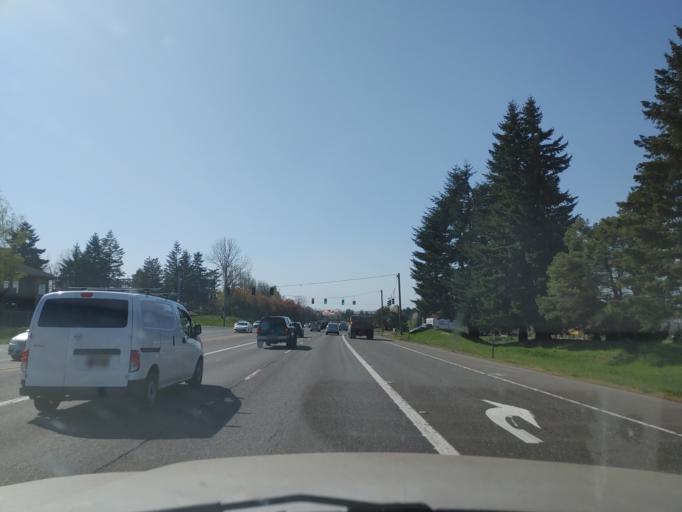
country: US
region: Oregon
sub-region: Clackamas County
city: Clackamas
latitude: 45.4225
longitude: -122.5809
